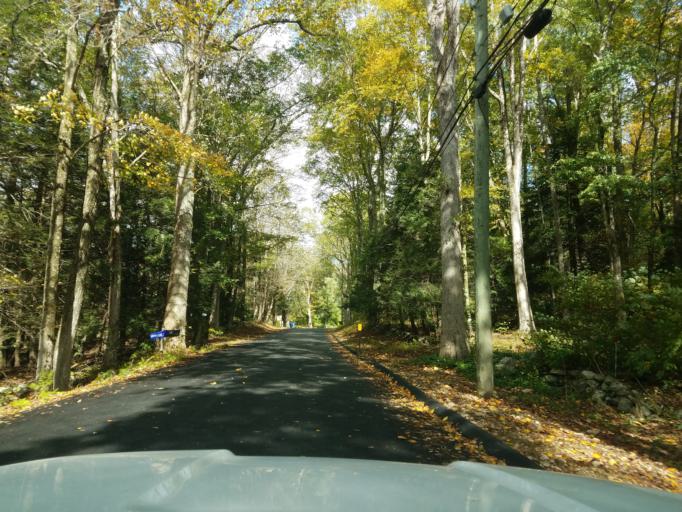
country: US
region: Connecticut
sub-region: Tolland County
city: South Coventry
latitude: 41.7169
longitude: -72.2913
